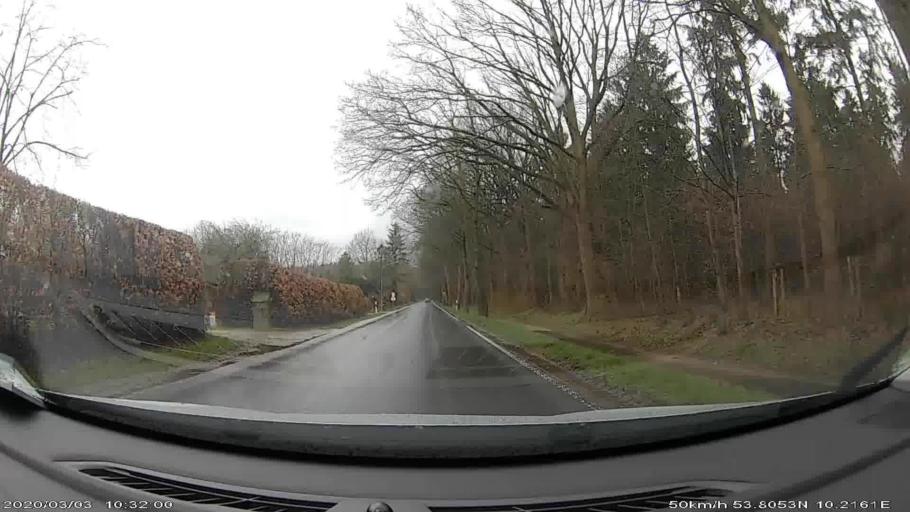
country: DE
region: Schleswig-Holstein
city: Sulfeld
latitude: 53.8068
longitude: 10.2110
